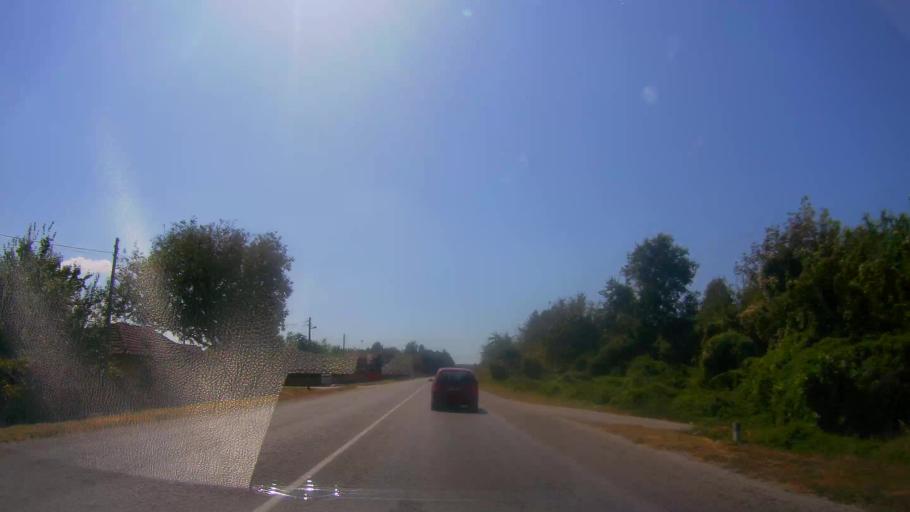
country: BG
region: Veliko Turnovo
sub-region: Obshtina Polski Trumbesh
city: Polski Trumbesh
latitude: 43.2679
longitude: 25.6436
